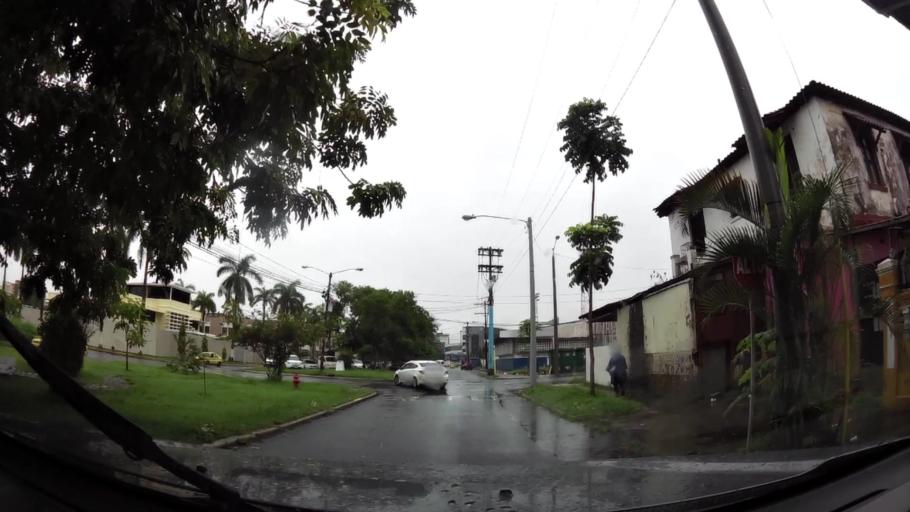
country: PA
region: Colon
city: Colon
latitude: 9.3577
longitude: -79.8955
